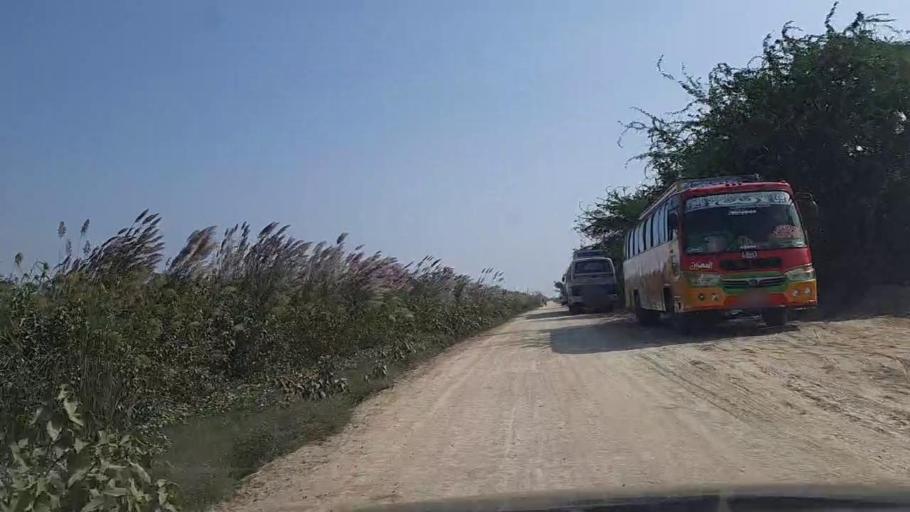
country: PK
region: Sindh
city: Gharo
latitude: 24.7206
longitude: 67.5574
